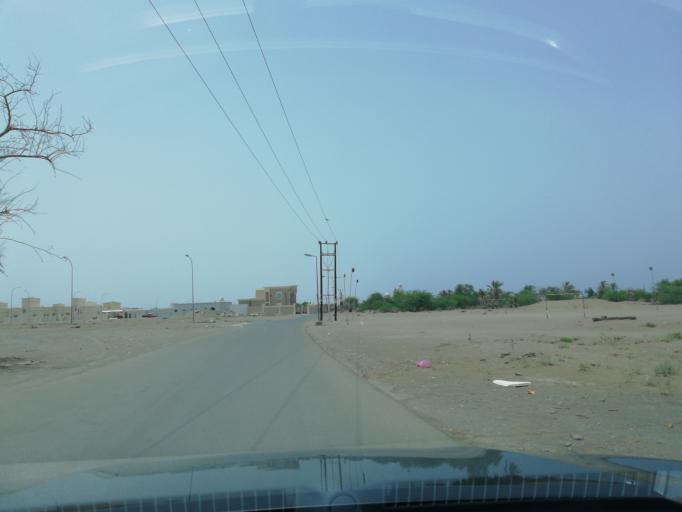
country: OM
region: Al Batinah
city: Al Liwa'
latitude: 24.6135
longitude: 56.5367
